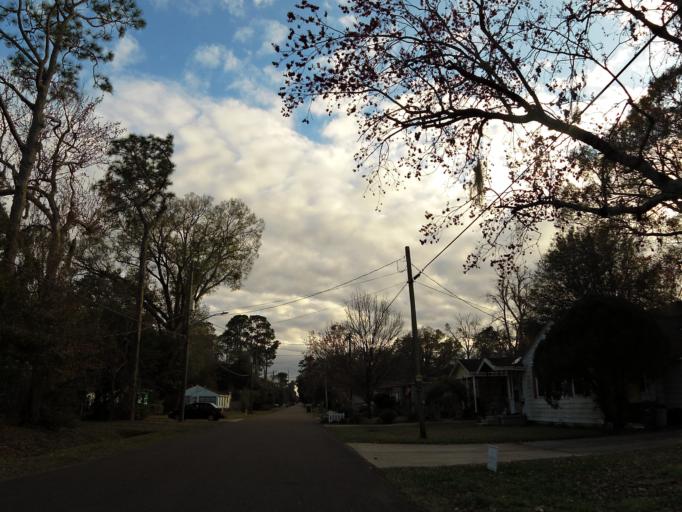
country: US
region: Florida
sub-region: Duval County
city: Jacksonville
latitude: 30.3060
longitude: -81.7263
